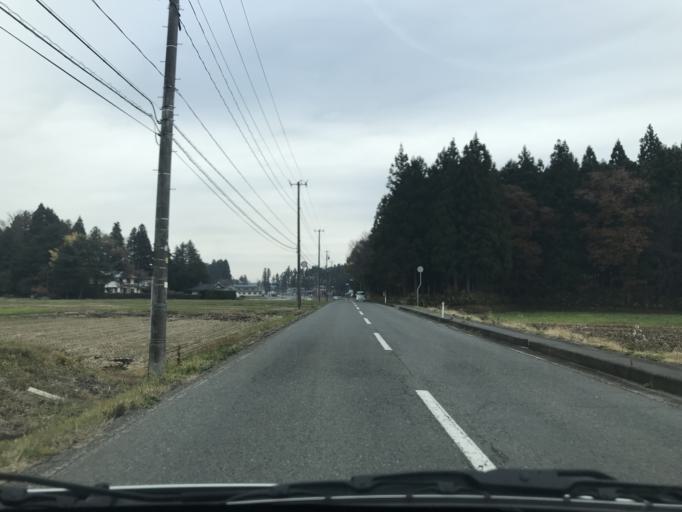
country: JP
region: Iwate
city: Mizusawa
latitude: 39.1074
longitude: 141.1081
